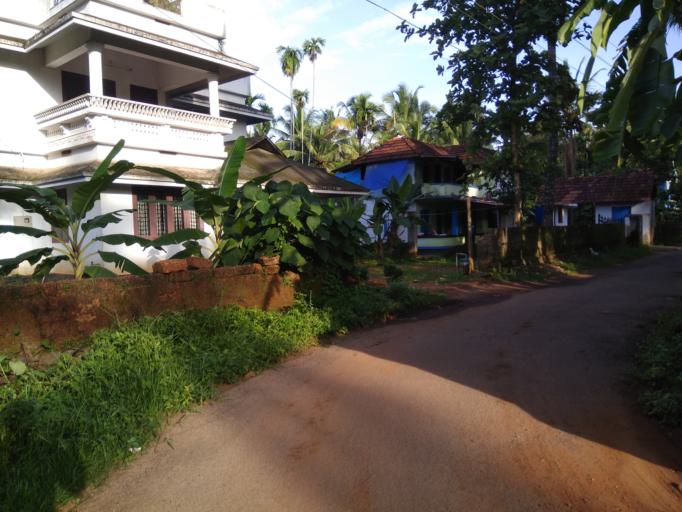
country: IN
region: Kerala
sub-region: Thrissur District
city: Avanoor
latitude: 10.5595
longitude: 76.1743
